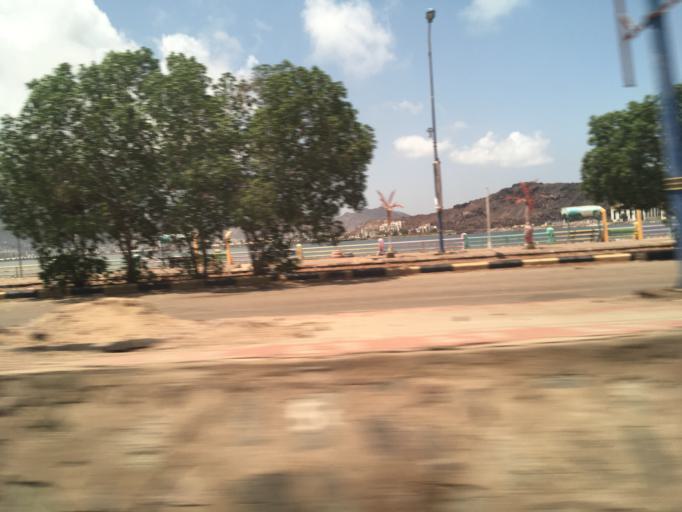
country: YE
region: Aden
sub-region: Khur Maksar
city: Khawr Maksar
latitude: 12.8089
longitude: 45.0253
